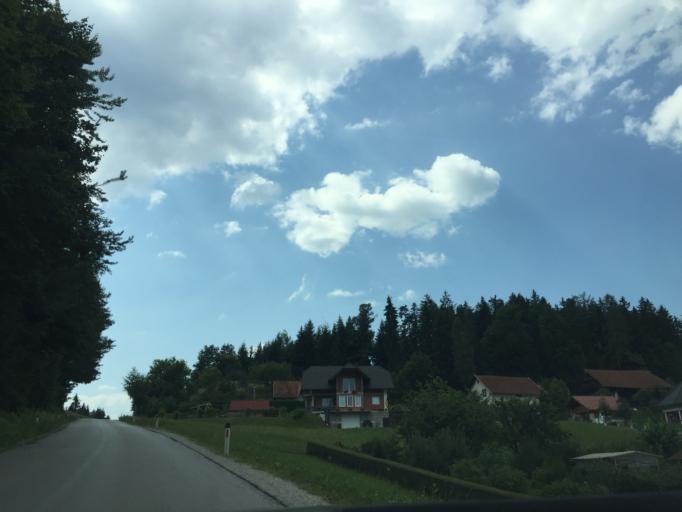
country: SI
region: Velenje
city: Velenje
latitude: 46.3860
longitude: 15.1039
